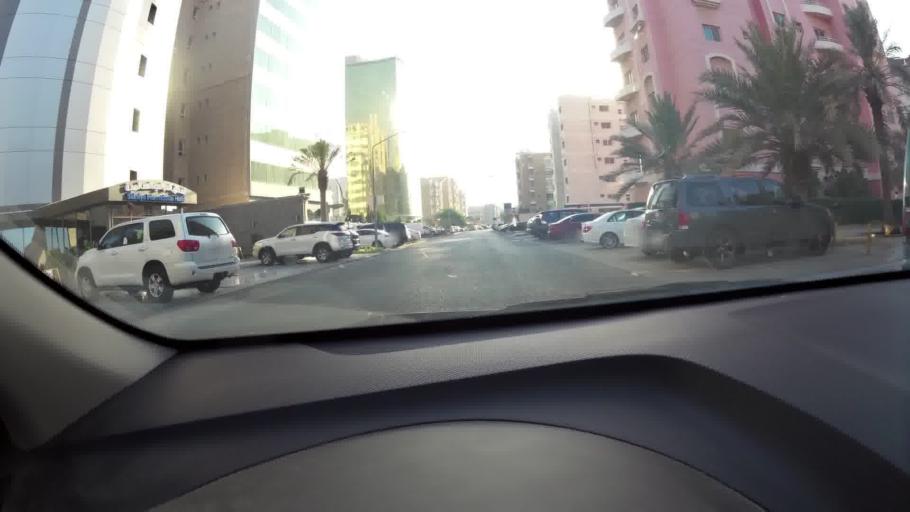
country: KW
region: Muhafazat Hawalli
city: As Salimiyah
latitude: 29.3384
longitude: 48.0730
